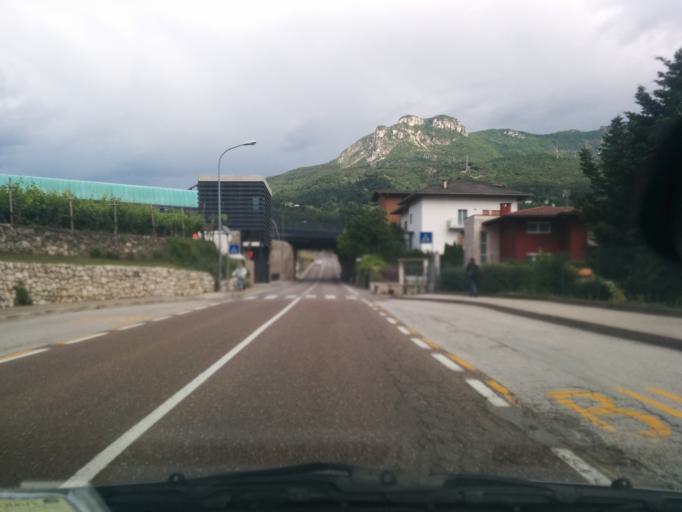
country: IT
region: Trentino-Alto Adige
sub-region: Provincia di Trento
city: Povo
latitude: 46.0650
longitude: 11.1416
